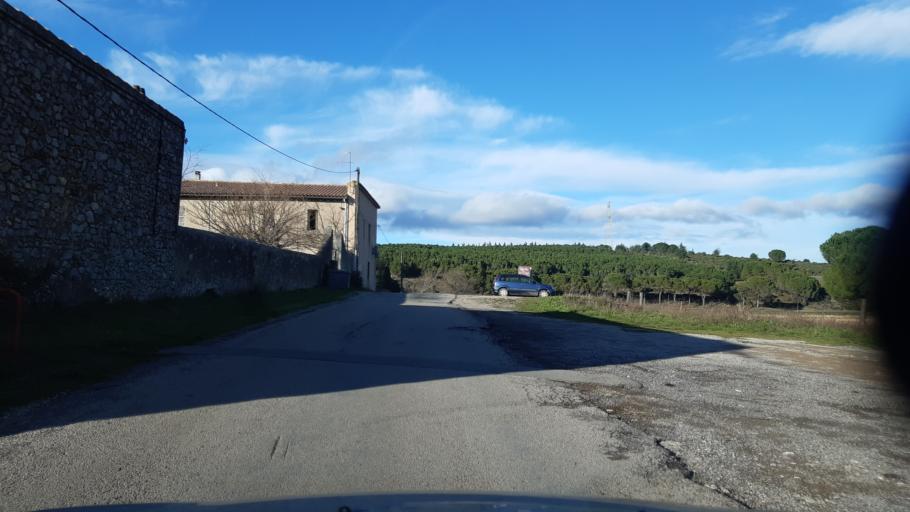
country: FR
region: Languedoc-Roussillon
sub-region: Departement de l'Herault
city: Murviel-les-Montpellier
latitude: 43.6251
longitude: 3.7392
